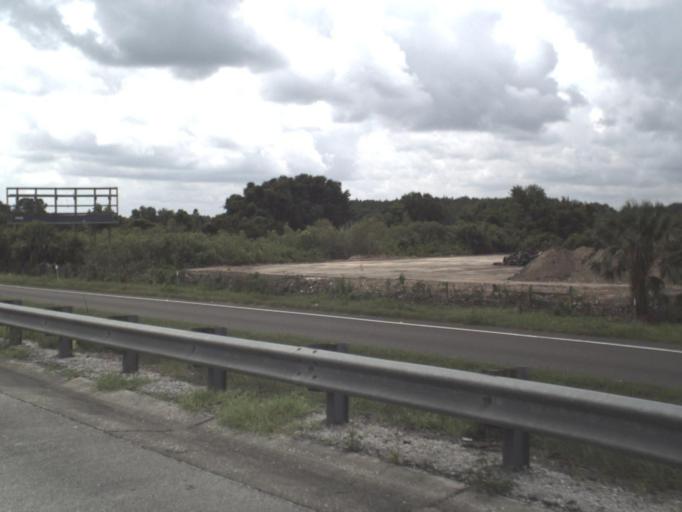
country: US
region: Florida
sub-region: Pasco County
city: San Antonio
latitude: 28.3238
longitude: -82.3249
